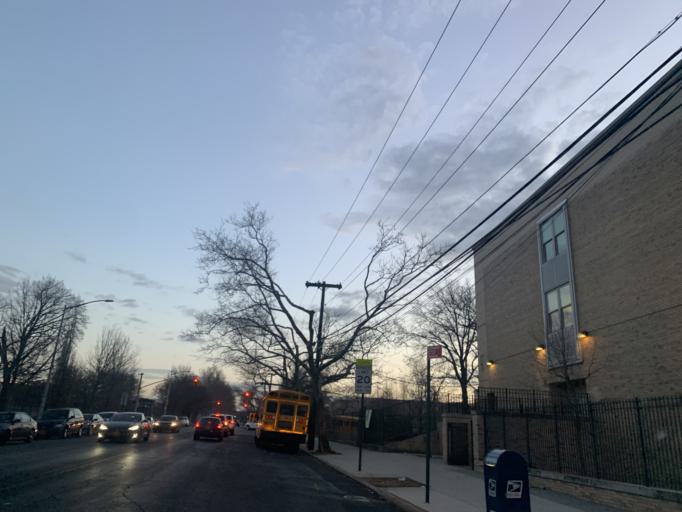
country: US
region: New York
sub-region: Nassau County
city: East Atlantic Beach
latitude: 40.7753
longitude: -73.8176
